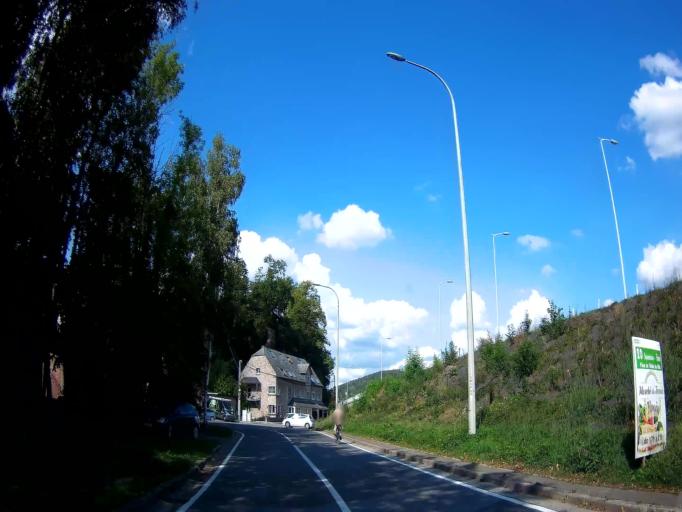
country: BE
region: Wallonia
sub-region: Province de Namur
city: Anhee
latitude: 50.3153
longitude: 4.8756
